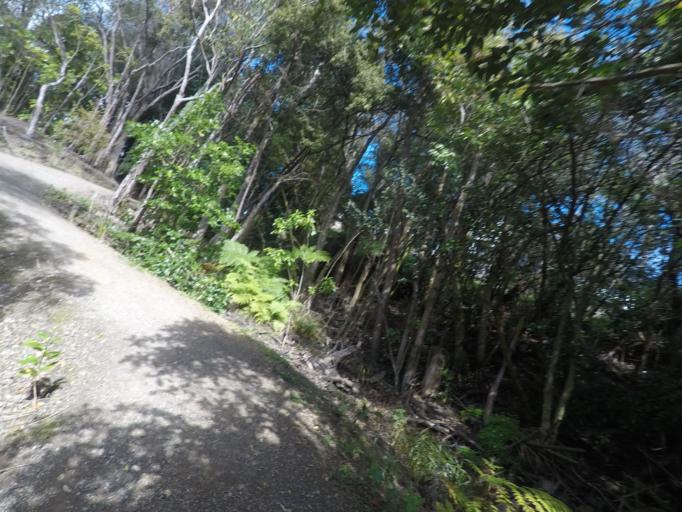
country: NZ
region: Auckland
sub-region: Auckland
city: Rosebank
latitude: -36.8572
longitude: 174.7161
